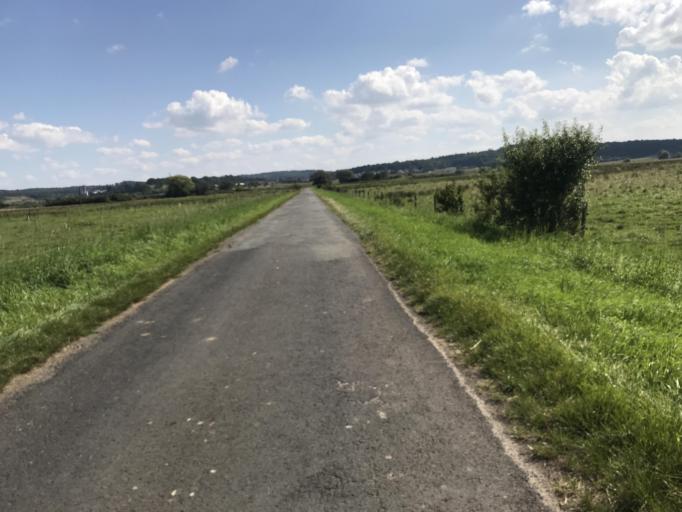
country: DE
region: Hesse
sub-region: Regierungsbezirk Giessen
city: Hungen
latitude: 50.4350
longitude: 8.8985
